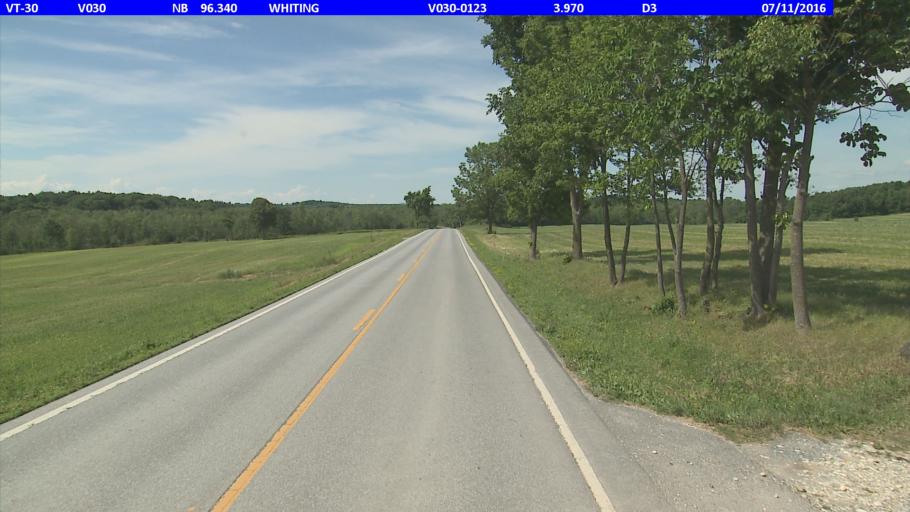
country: US
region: Vermont
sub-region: Addison County
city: Middlebury (village)
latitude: 43.8945
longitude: -73.2031
